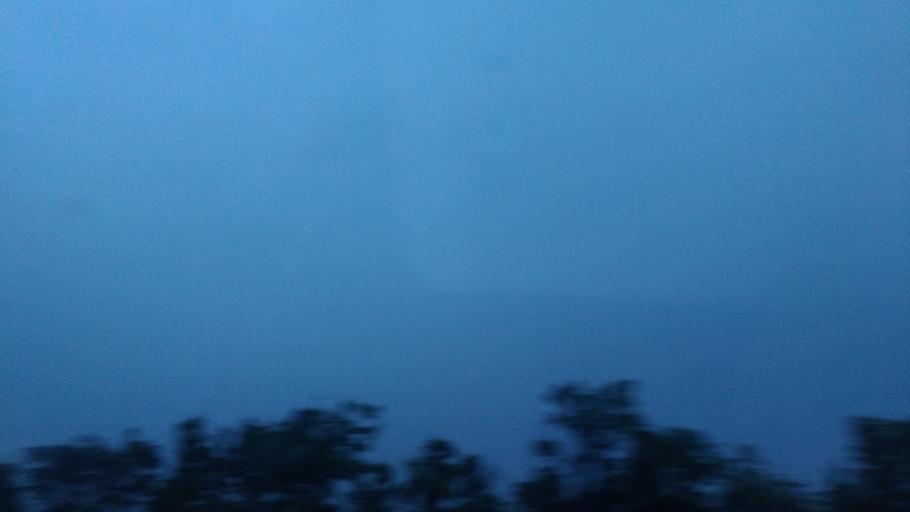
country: TW
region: Taiwan
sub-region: Miaoli
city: Miaoli
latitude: 24.5990
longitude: 120.7426
